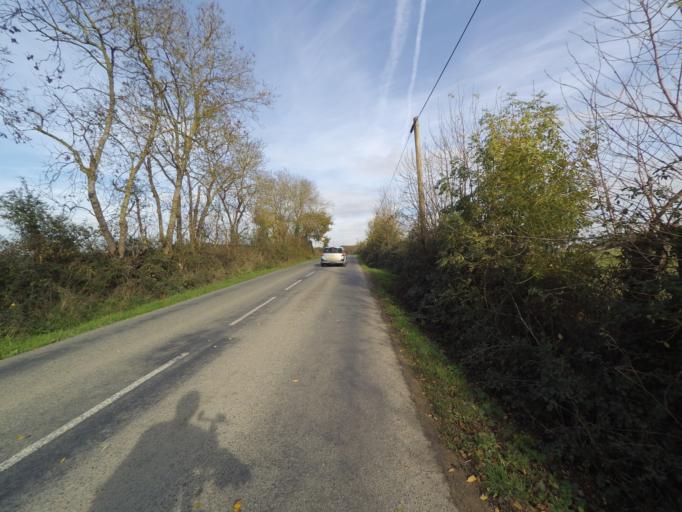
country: FR
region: Pays de la Loire
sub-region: Departement de la Vendee
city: Saint-Hilaire-de-Loulay
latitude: 47.0124
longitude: -1.3528
